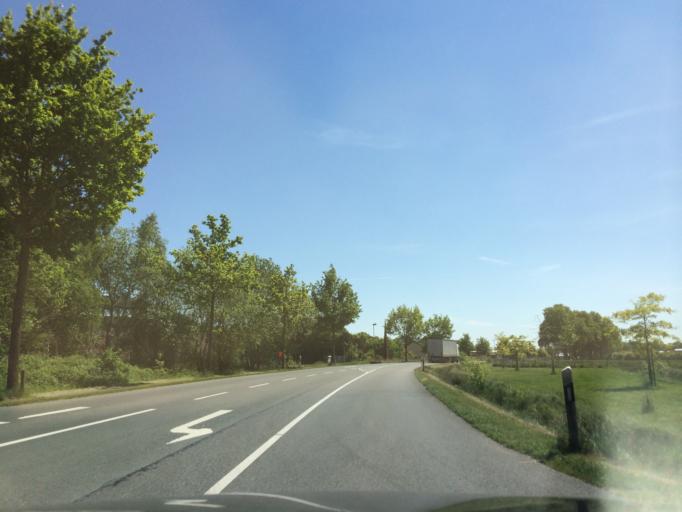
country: DE
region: Lower Saxony
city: Ganderkesee
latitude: 53.0409
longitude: 8.5198
